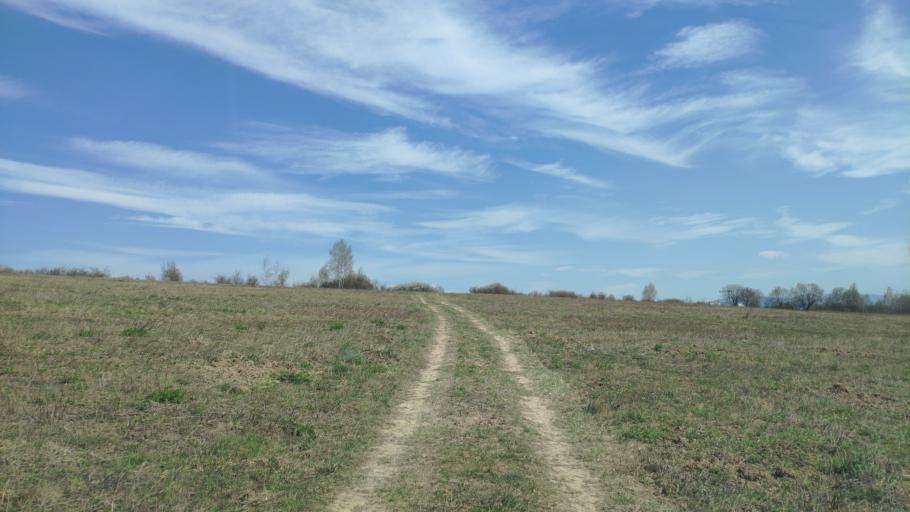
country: SK
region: Kosicky
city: Kosice
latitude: 48.7236
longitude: 21.1942
